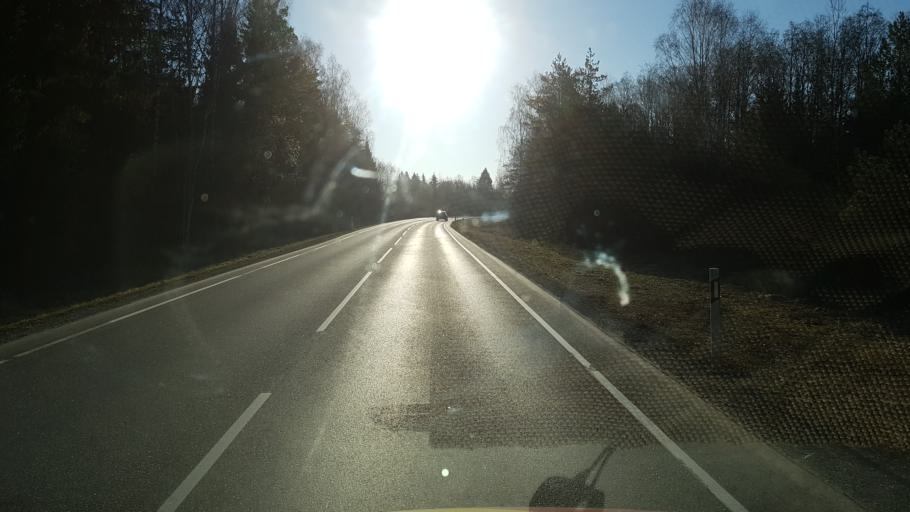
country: EE
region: Raplamaa
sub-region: Kehtna vald
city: Kehtna
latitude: 58.8852
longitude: 24.9624
